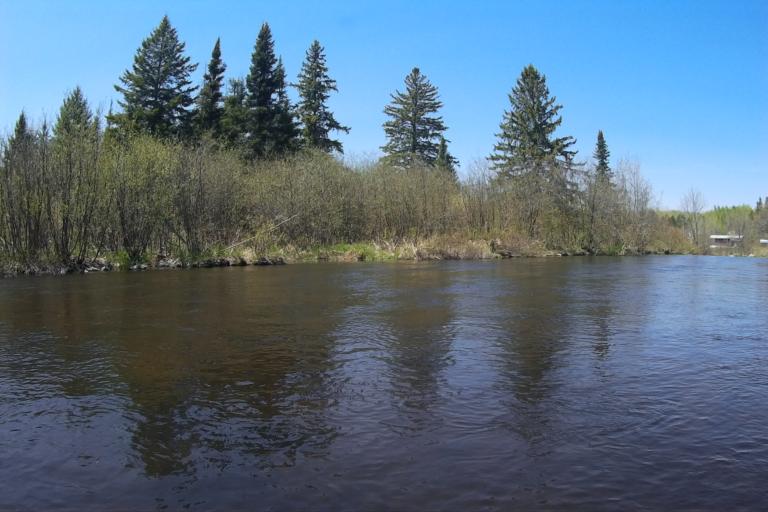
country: CA
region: Ontario
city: Powassan
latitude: 46.1609
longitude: -79.2585
